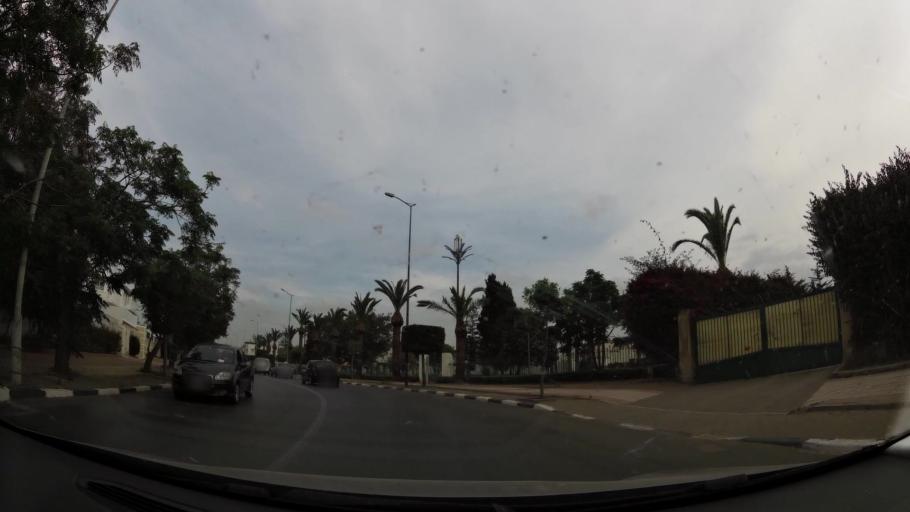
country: MA
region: Rabat-Sale-Zemmour-Zaer
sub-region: Rabat
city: Rabat
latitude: 34.0310
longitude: -6.8145
